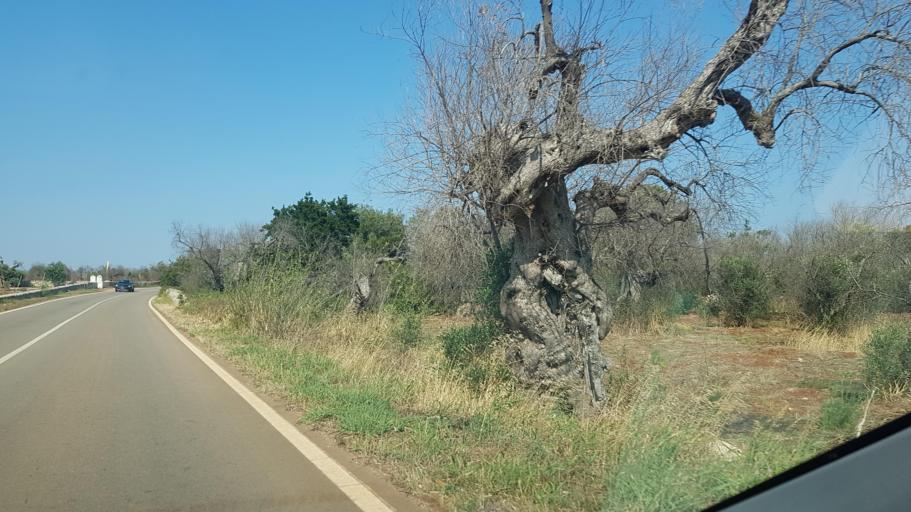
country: IT
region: Apulia
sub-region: Provincia di Lecce
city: Acquarica del Capo
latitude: 39.8896
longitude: 18.2436
